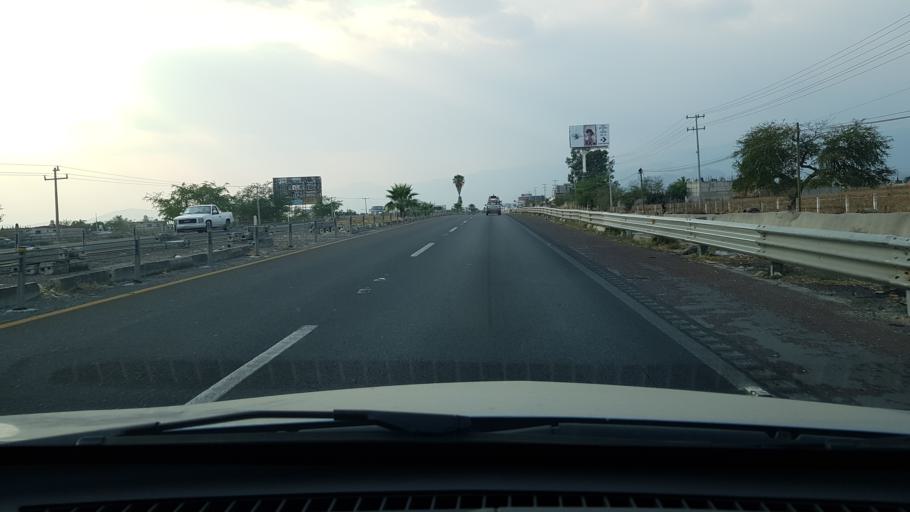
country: MX
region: Morelos
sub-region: Cuautla
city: Tierra Larga (Campo Nuevo)
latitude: 18.8591
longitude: -98.9442
